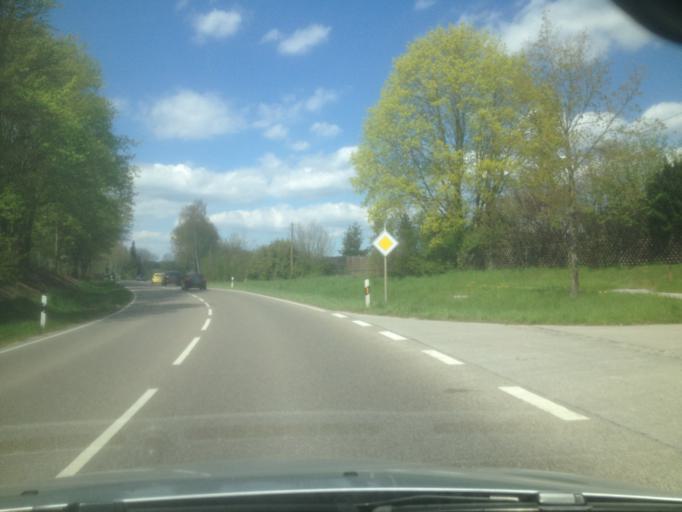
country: DE
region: Bavaria
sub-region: Swabia
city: Diedorf
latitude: 48.3696
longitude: 10.7949
